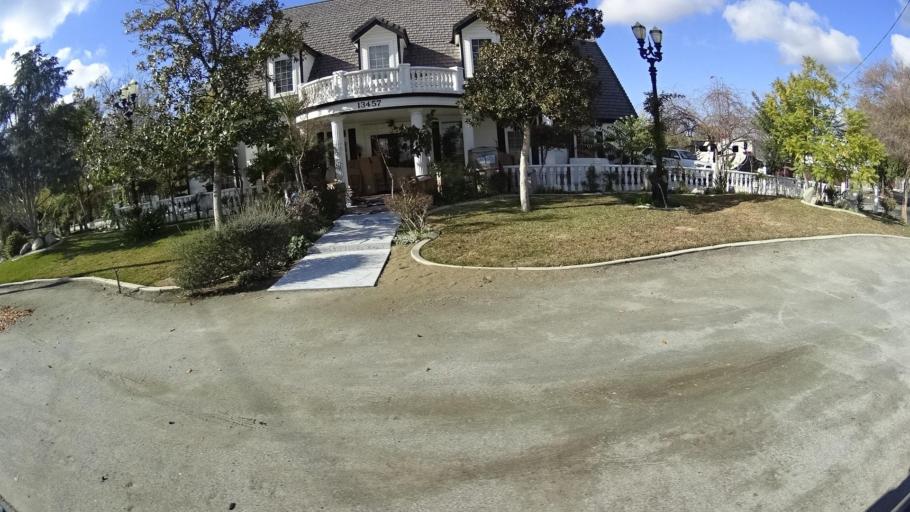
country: US
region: California
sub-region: Kern County
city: McFarland
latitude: 35.6629
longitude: -119.2410
